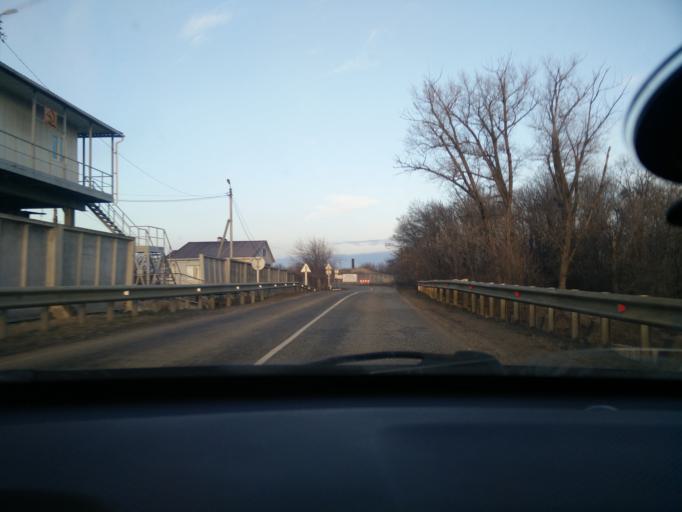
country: RU
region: Stavropol'skiy
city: Balakhonovskoye
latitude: 44.9798
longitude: 41.6906
